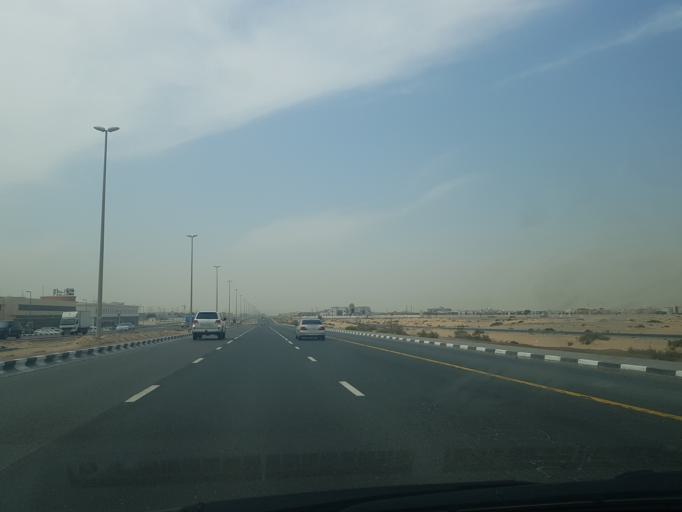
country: AE
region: Ash Shariqah
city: Sharjah
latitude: 25.2577
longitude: 55.5157
